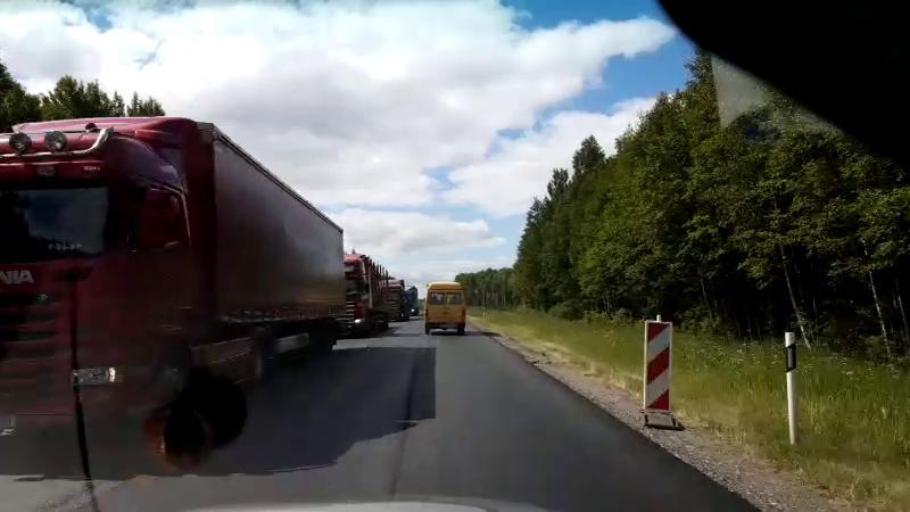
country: LV
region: Salacgrivas
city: Ainazi
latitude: 57.9849
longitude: 24.4631
